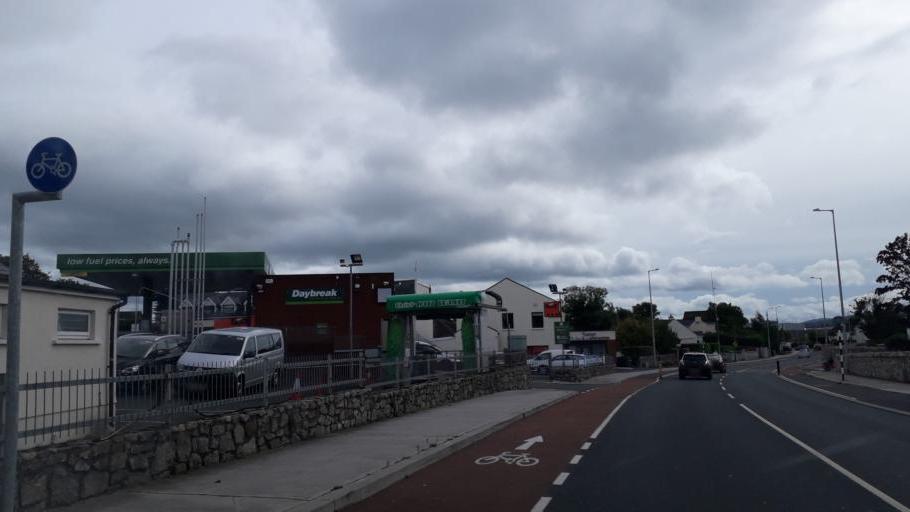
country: IE
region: Leinster
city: Cabinteely
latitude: 53.2795
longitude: -6.1577
